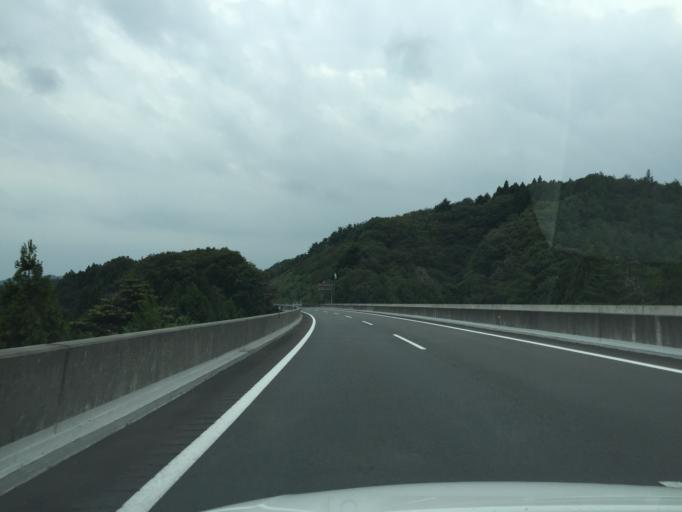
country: JP
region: Fukushima
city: Iwaki
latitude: 37.0835
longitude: 140.7876
